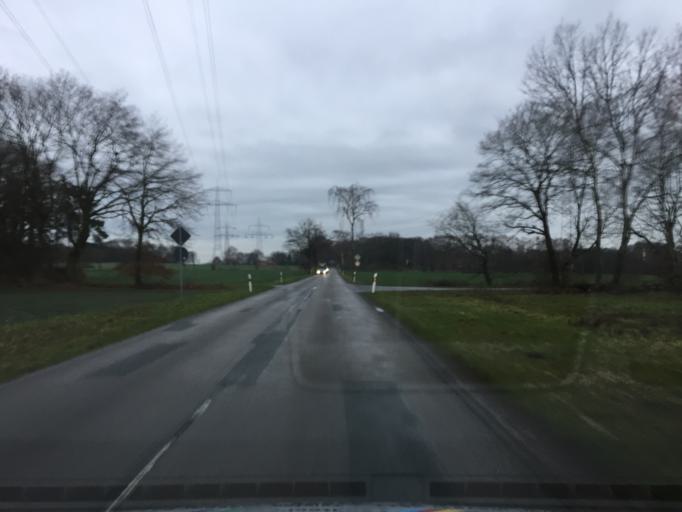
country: DE
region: Lower Saxony
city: Pennigsehl
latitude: 52.6197
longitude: 8.9954
